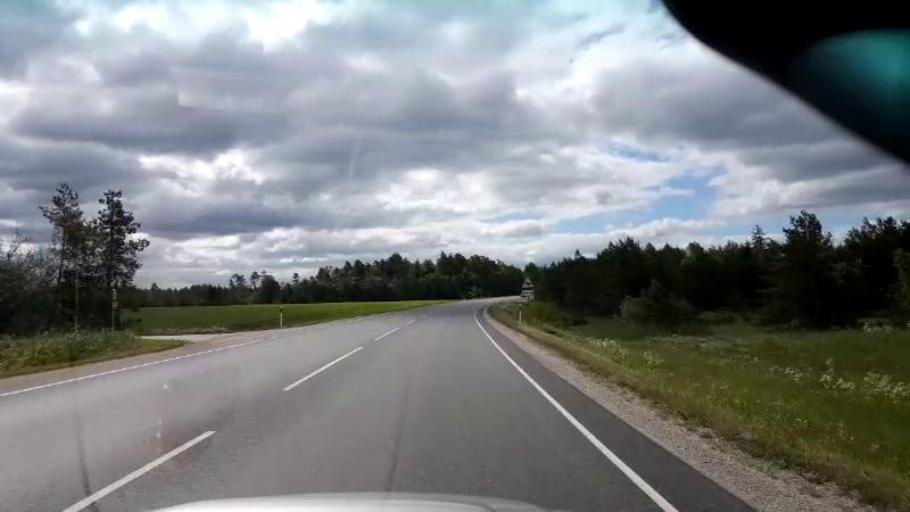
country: EE
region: Paernumaa
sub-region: Halinga vald
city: Parnu-Jaagupi
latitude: 58.6824
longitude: 24.4427
